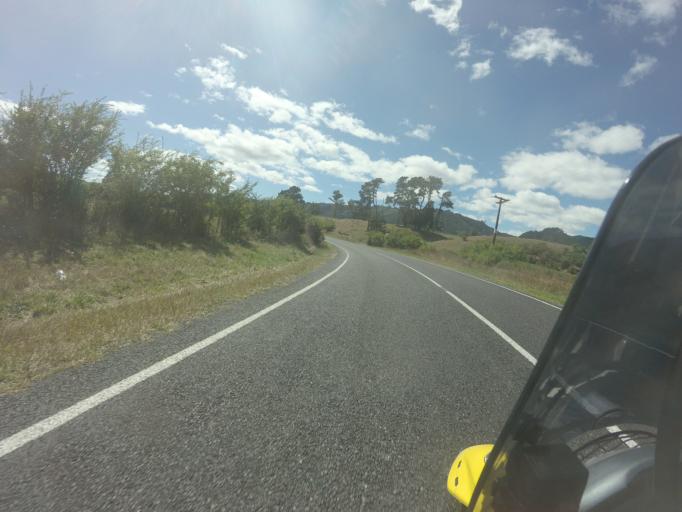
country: NZ
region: Bay of Plenty
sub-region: Kawerau District
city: Kawerau
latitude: -38.2335
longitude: 176.8378
